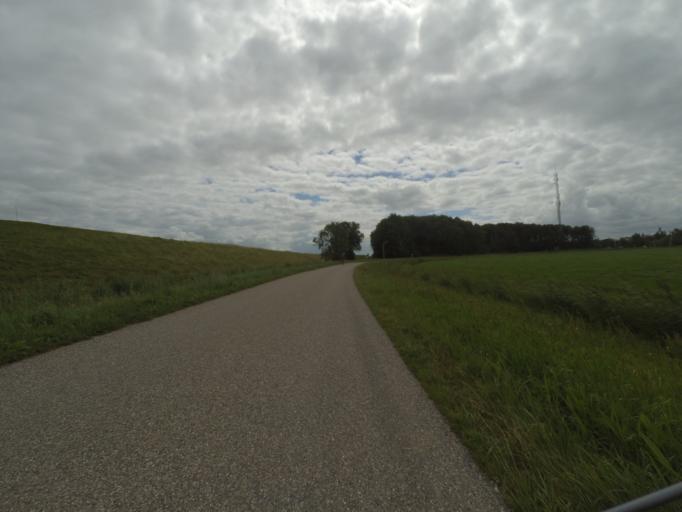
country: NL
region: Friesland
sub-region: Gemeente Kollumerland en Nieuwkruisland
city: Kollum
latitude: 53.3269
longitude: 6.1549
